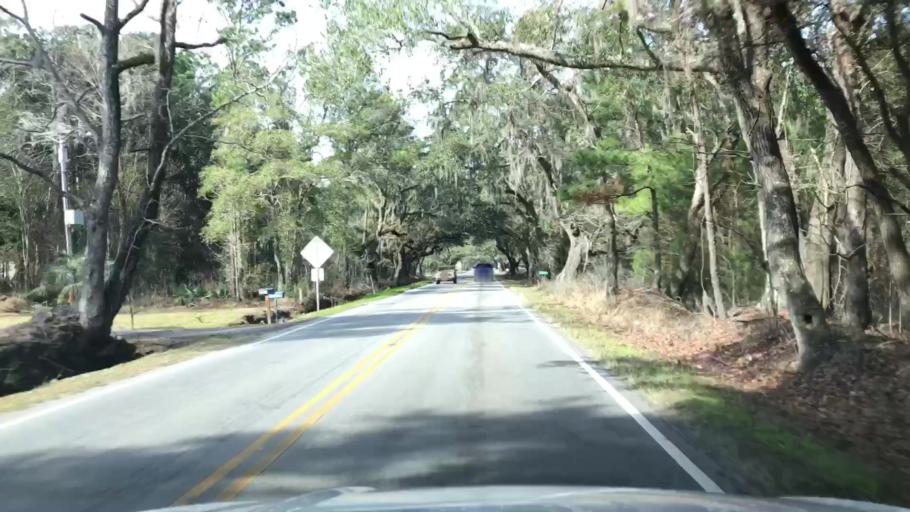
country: US
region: South Carolina
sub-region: Charleston County
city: Shell Point
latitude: 32.7536
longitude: -80.0469
